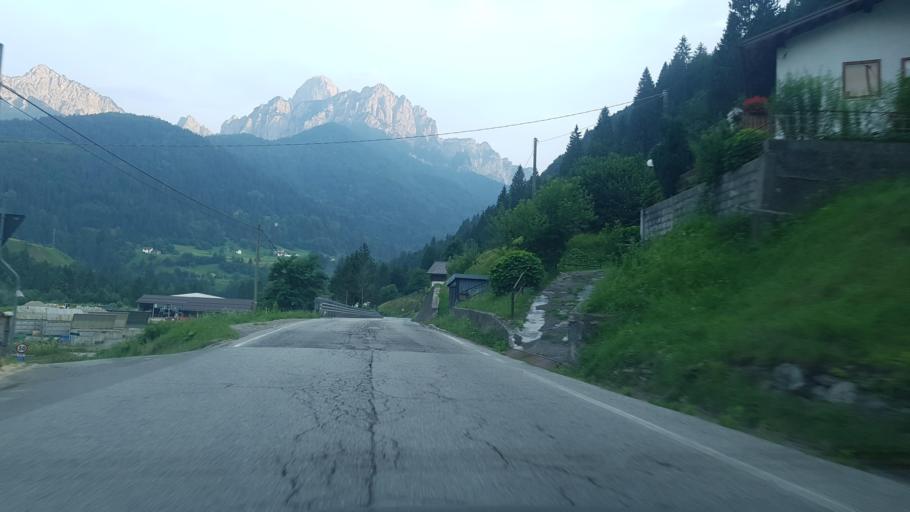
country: IT
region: Friuli Venezia Giulia
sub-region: Provincia di Udine
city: Paularo
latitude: 46.5199
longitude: 13.1221
